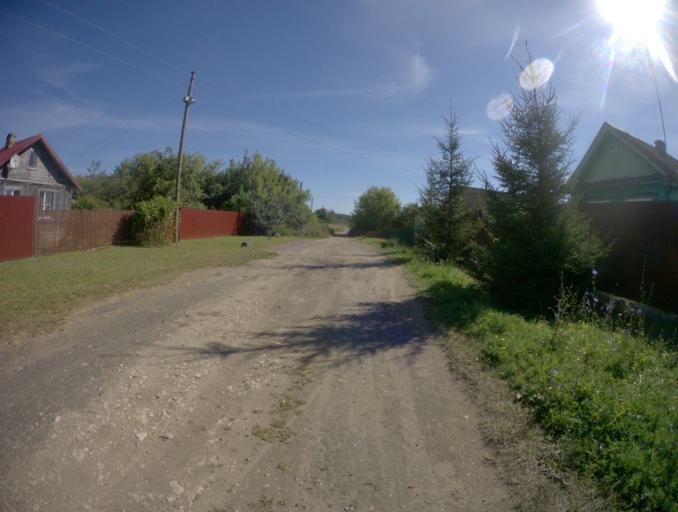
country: RU
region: Vladimir
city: Nikologory
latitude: 56.0978
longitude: 41.9254
